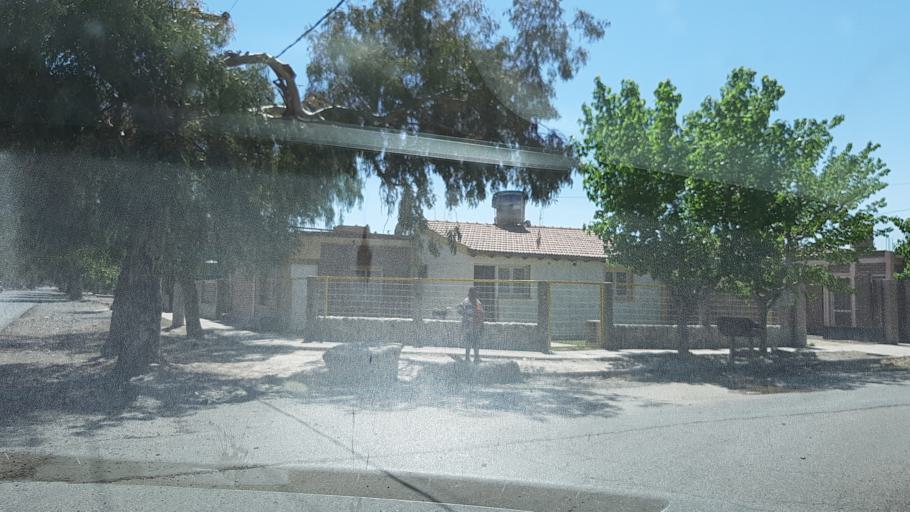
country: AR
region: San Juan
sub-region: Departamento de Zonda
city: Zonda
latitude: -31.5397
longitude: -68.7523
